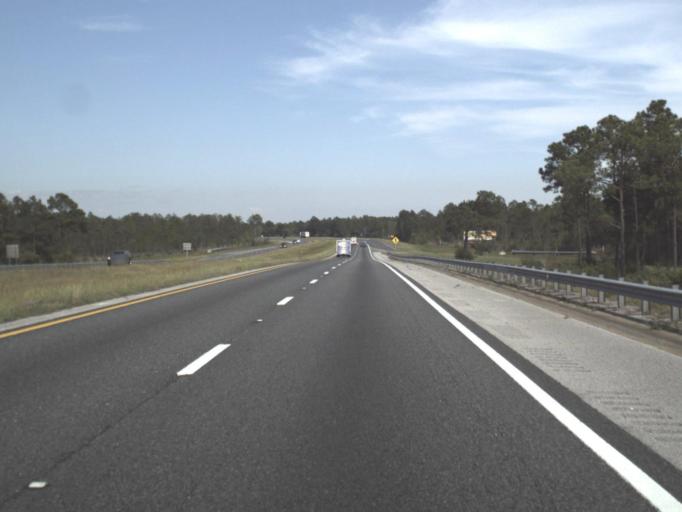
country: US
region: Florida
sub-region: Santa Rosa County
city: Bagdad
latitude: 30.5338
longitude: -87.0862
